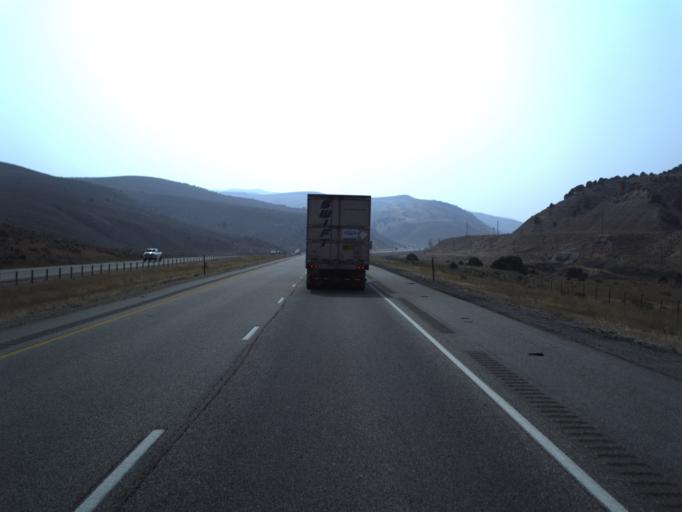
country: US
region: Utah
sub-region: Summit County
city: Coalville
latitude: 41.0965
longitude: -111.2192
